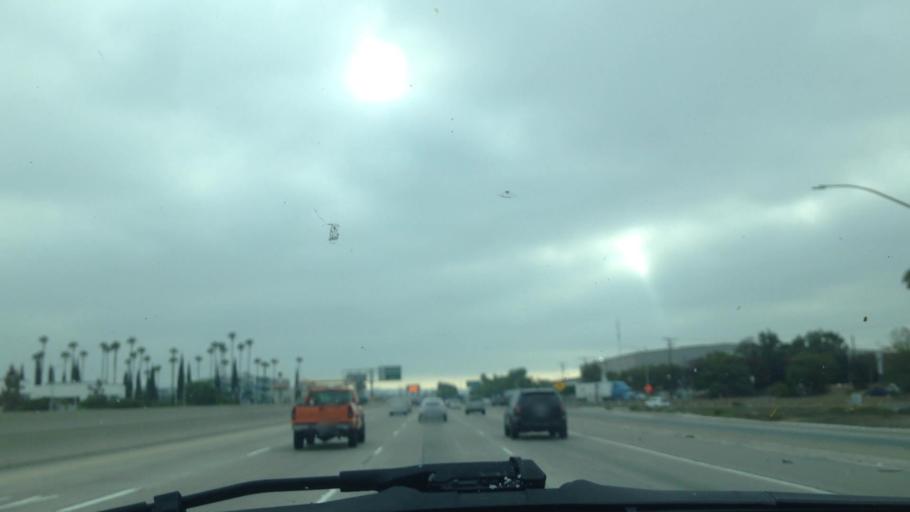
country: US
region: California
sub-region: Orange County
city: Placentia
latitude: 33.8479
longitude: -117.8542
